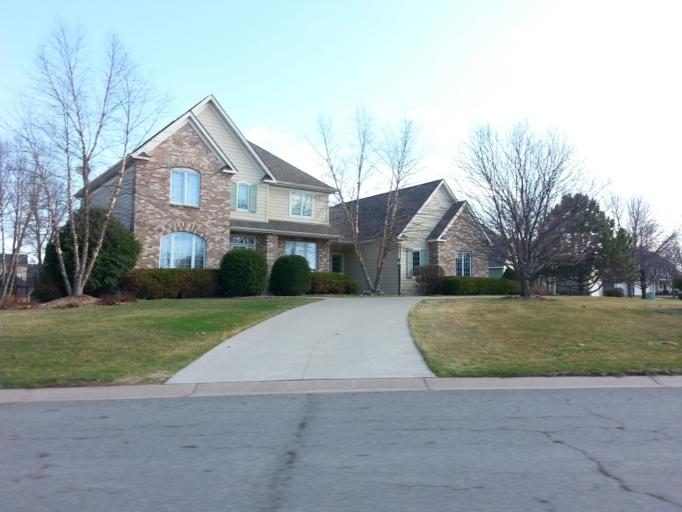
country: US
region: Minnesota
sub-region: Washington County
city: Woodbury
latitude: 44.8992
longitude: -92.8965
